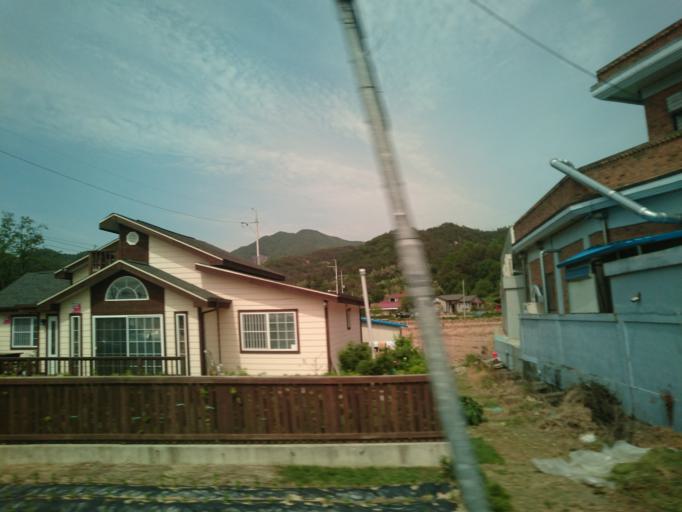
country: KR
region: Jeollabuk-do
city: Wanju
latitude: 35.8955
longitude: 127.1923
